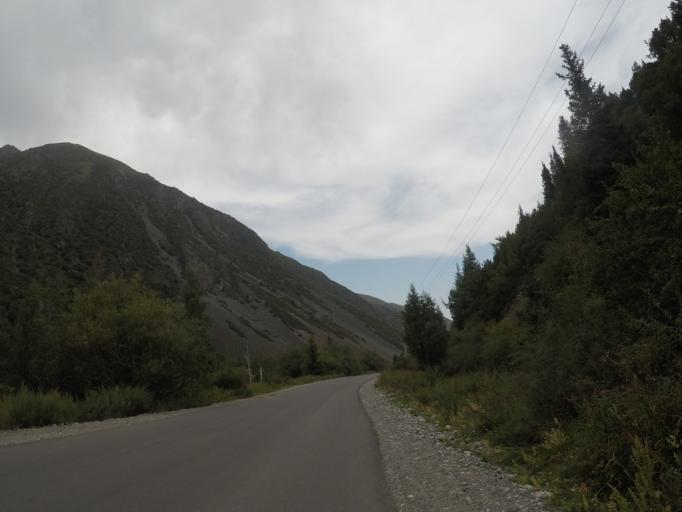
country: KG
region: Chuy
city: Bishkek
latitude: 42.5765
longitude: 74.4819
